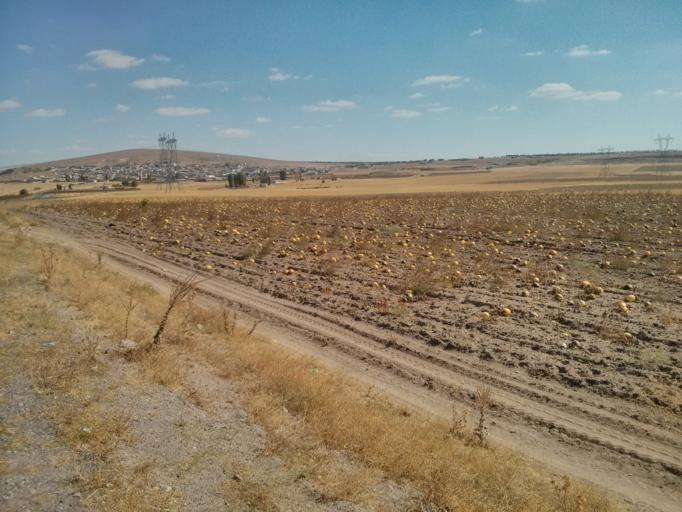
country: TR
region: Aksaray
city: Guzelyurt
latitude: 38.2474
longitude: 34.3125
